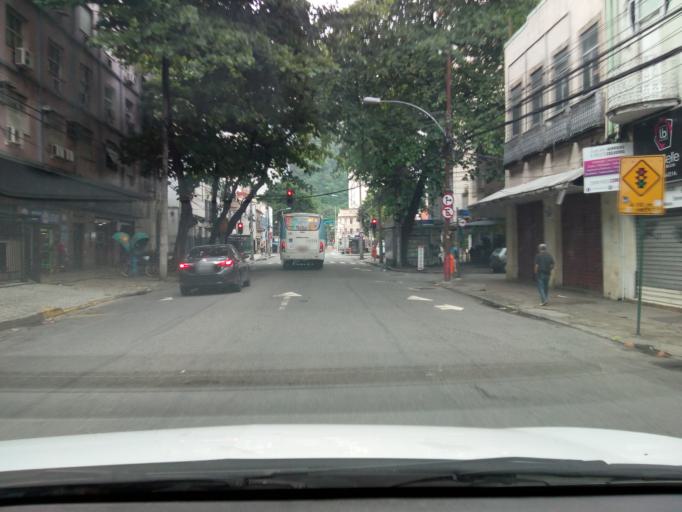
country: BR
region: Rio de Janeiro
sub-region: Rio De Janeiro
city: Rio de Janeiro
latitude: -22.9528
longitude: -43.1821
